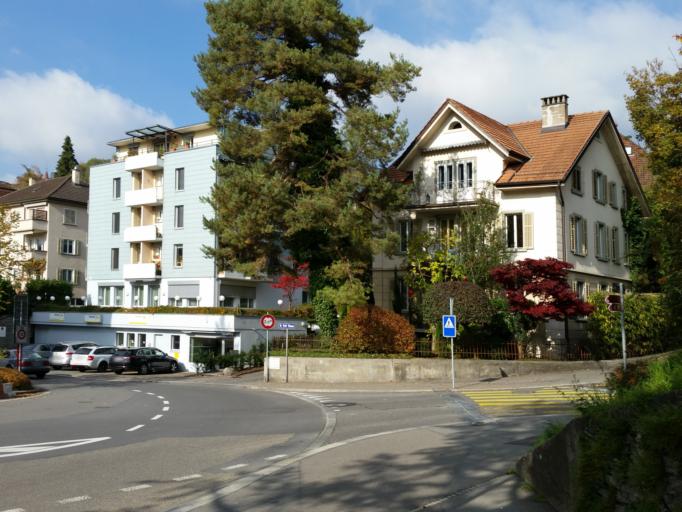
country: CH
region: Lucerne
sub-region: Lucerne-Stadt District
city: Luzern
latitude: 47.0538
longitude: 8.2996
